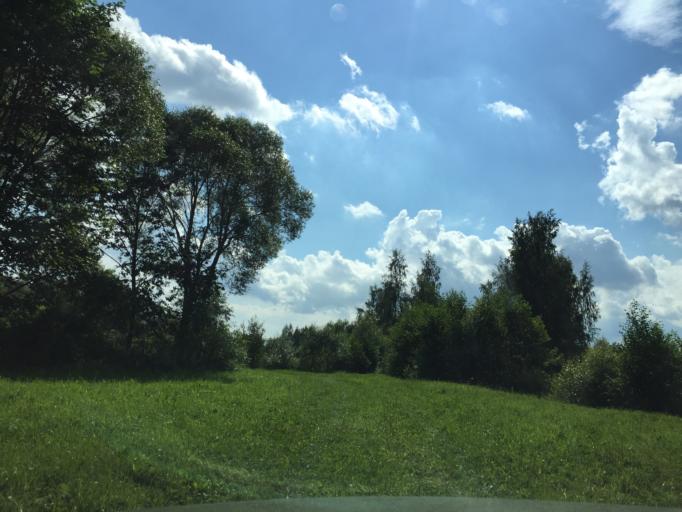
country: LV
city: Tervete
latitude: 56.6157
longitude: 23.4461
